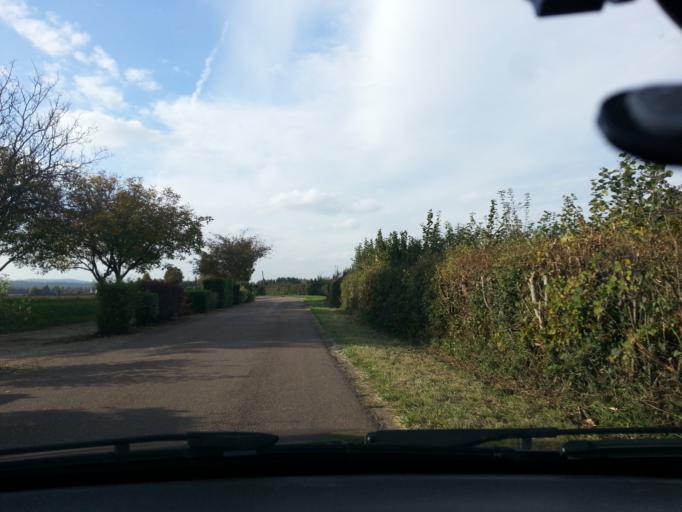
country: FR
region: Bourgogne
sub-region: Departement de Saone-et-Loire
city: Dracy-le-Fort
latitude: 46.7905
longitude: 4.7780
